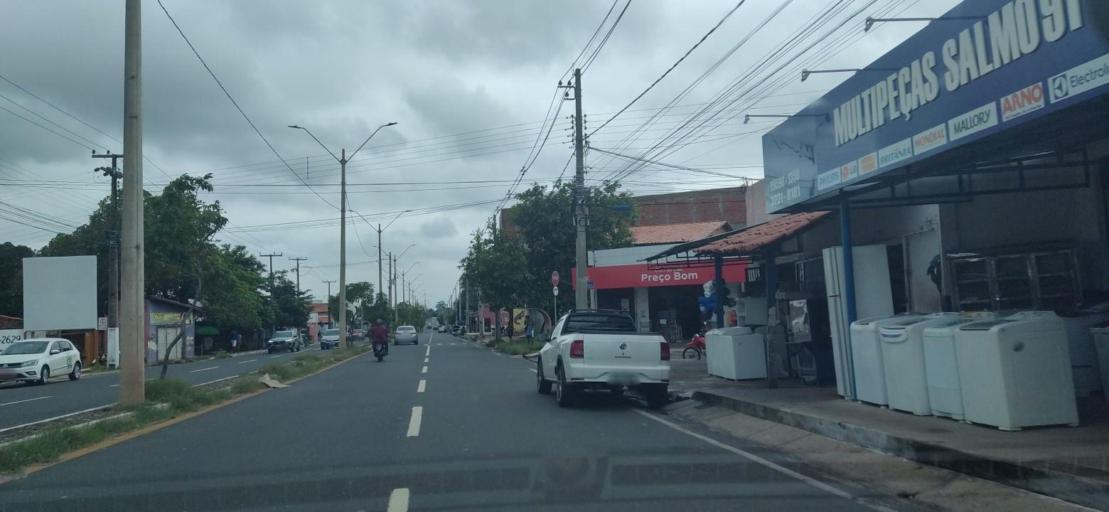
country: BR
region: Piaui
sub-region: Teresina
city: Teresina
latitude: -5.0525
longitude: -42.7431
